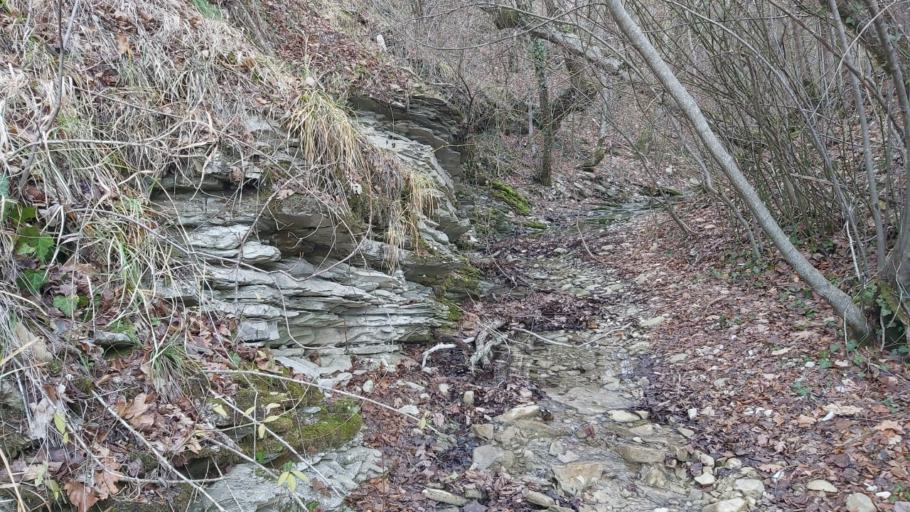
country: RU
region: Krasnodarskiy
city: Gelendzhik
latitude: 44.6100
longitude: 38.1400
